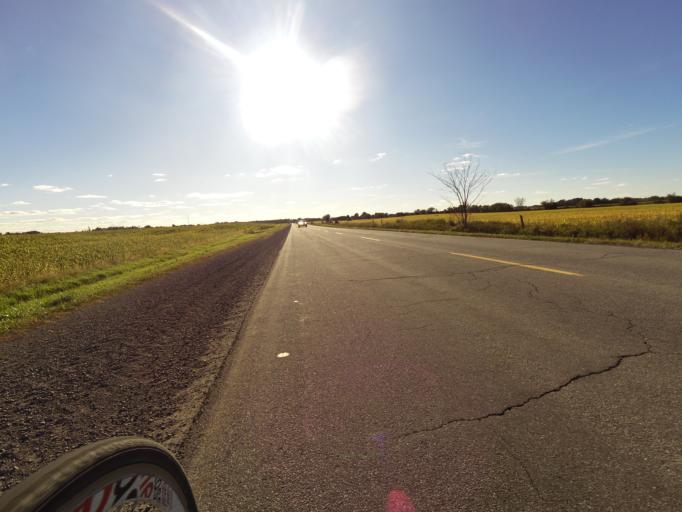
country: CA
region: Ontario
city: Bells Corners
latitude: 45.1854
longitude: -75.7967
